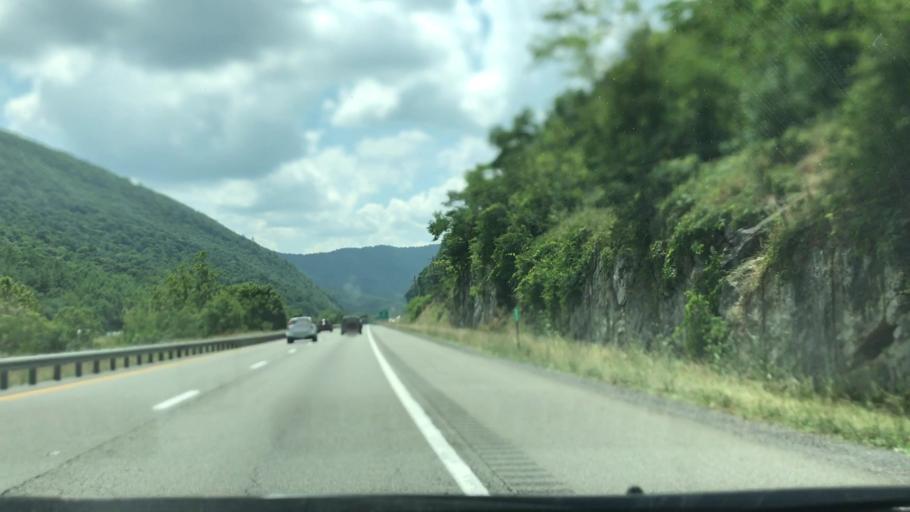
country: US
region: West Virginia
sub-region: Mercer County
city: Bluefield
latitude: 37.2348
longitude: -81.0976
